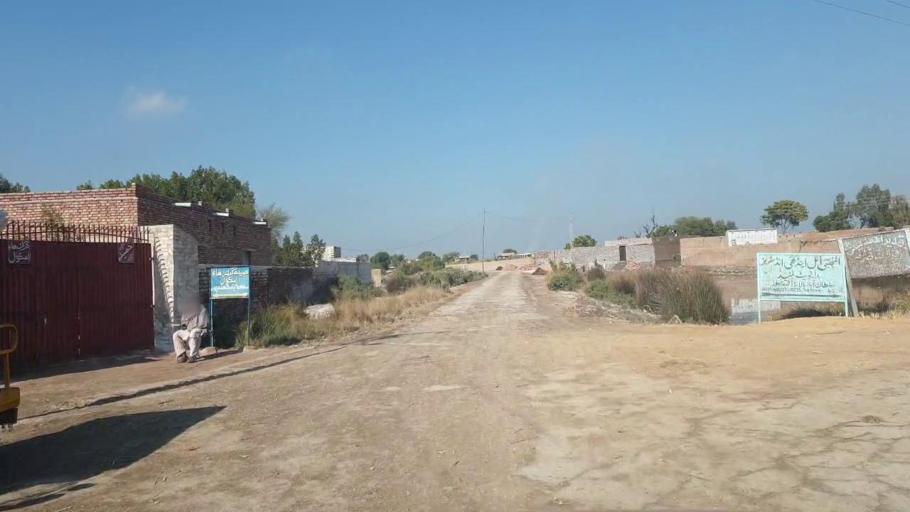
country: PK
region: Sindh
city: Shahdadpur
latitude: 25.9063
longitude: 68.5957
